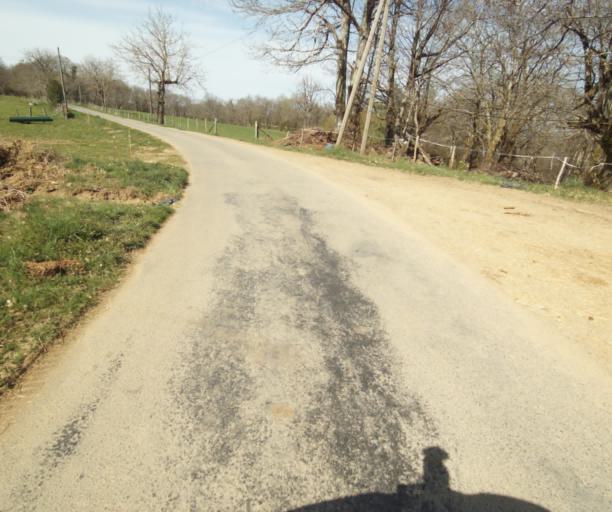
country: FR
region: Limousin
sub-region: Departement de la Correze
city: Naves
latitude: 45.3585
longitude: 1.7794
